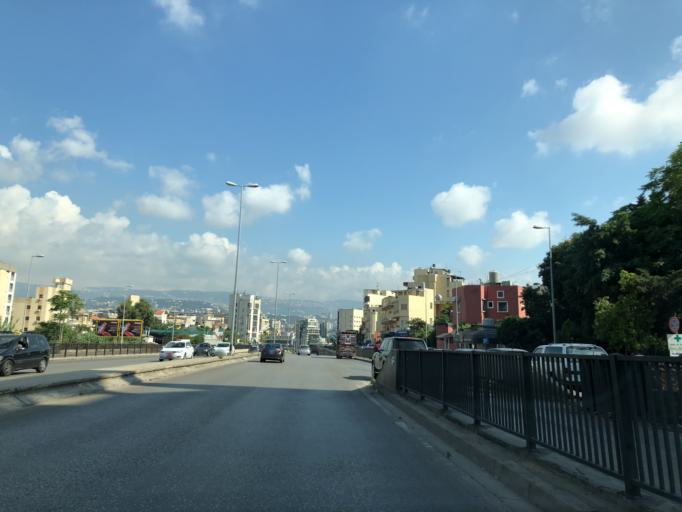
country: LB
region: Beyrouth
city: Beirut
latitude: 33.8751
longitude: 35.5238
